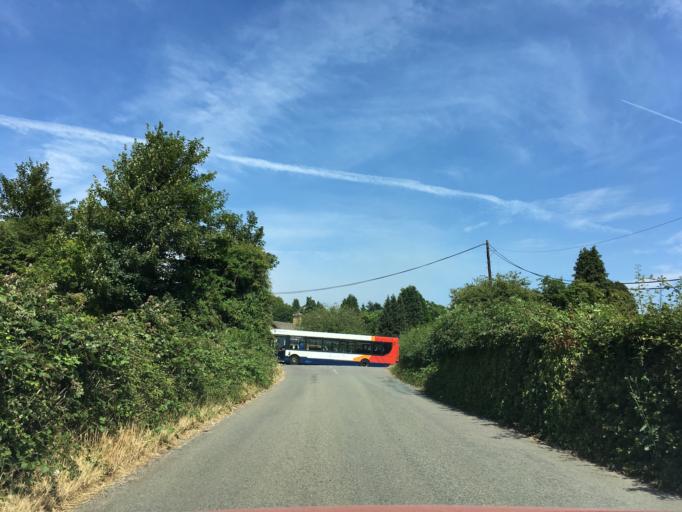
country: GB
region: Wales
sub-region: Caerphilly County Borough
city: Machen
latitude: 51.5847
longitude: -3.1195
